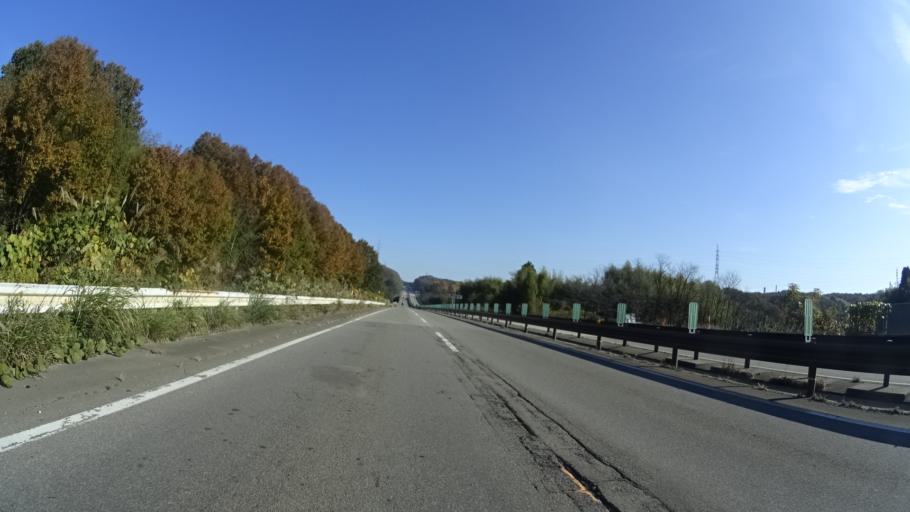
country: JP
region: Ishikawa
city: Komatsu
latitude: 36.3751
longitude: 136.4764
